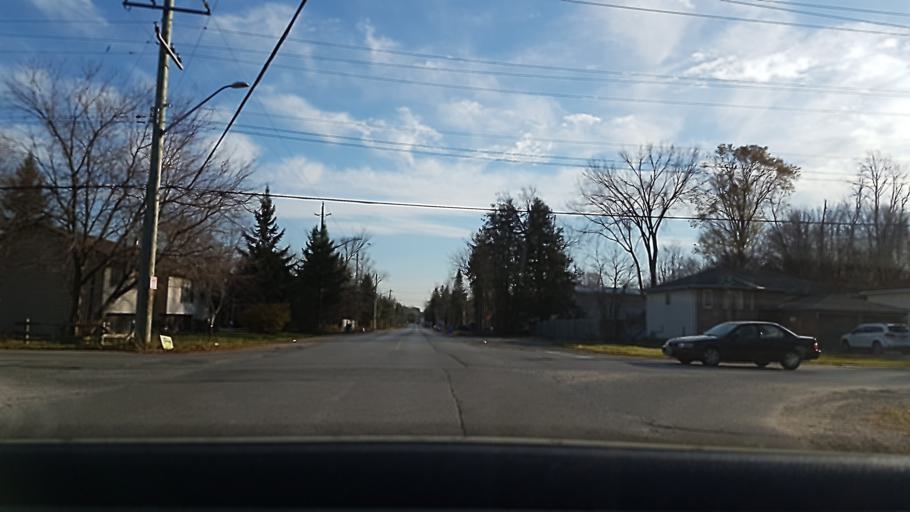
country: CA
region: Ontario
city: Innisfil
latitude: 44.3415
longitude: -79.5461
